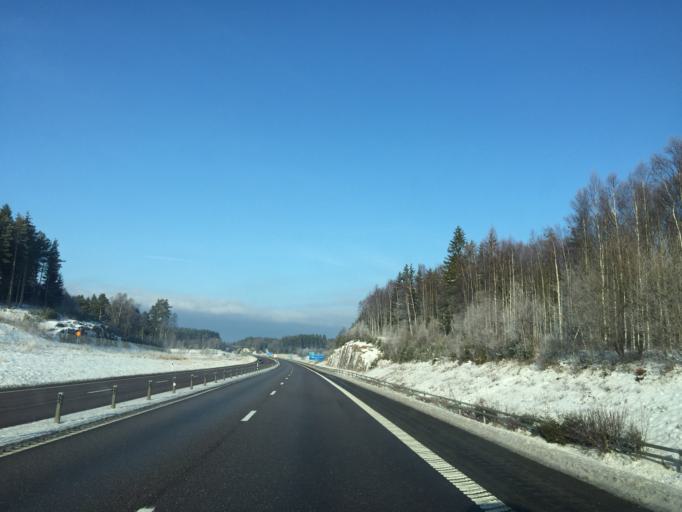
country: SE
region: Vaestra Goetaland
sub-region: Tanums Kommun
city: Tanumshede
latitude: 58.7248
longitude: 11.3491
